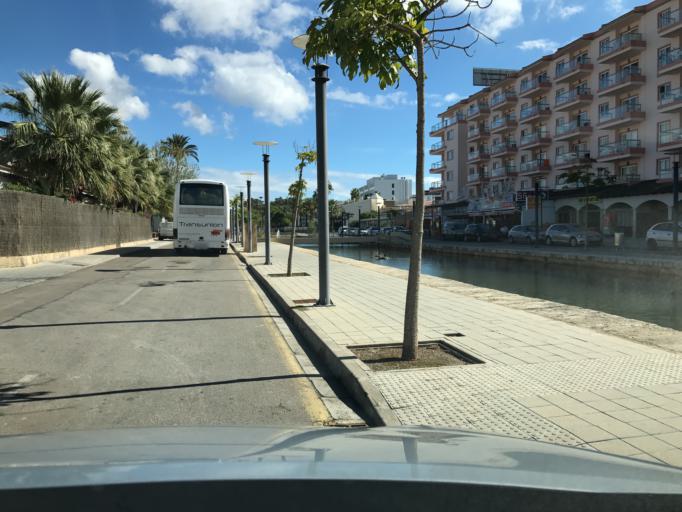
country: ES
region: Balearic Islands
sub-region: Illes Balears
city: Alcudia
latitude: 39.8340
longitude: 3.1134
